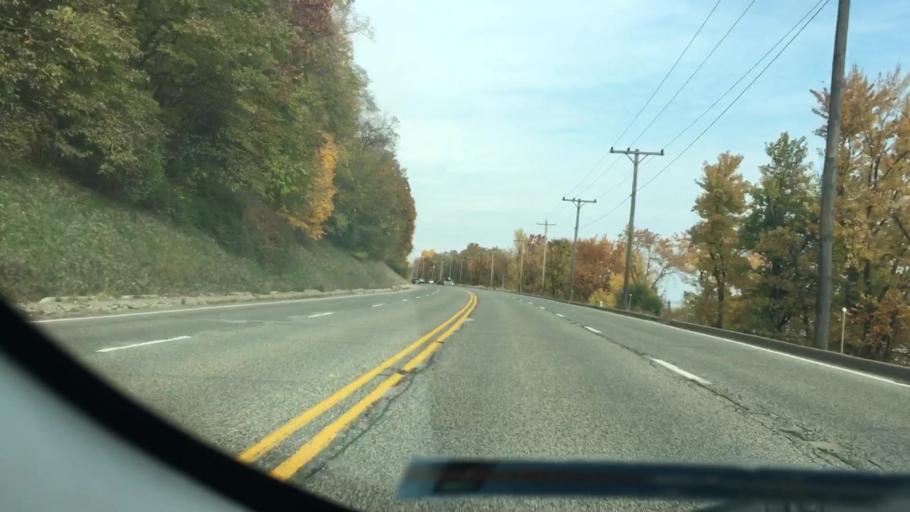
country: US
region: Illinois
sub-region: Peoria County
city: Peoria Heights
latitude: 40.7347
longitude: -89.5516
